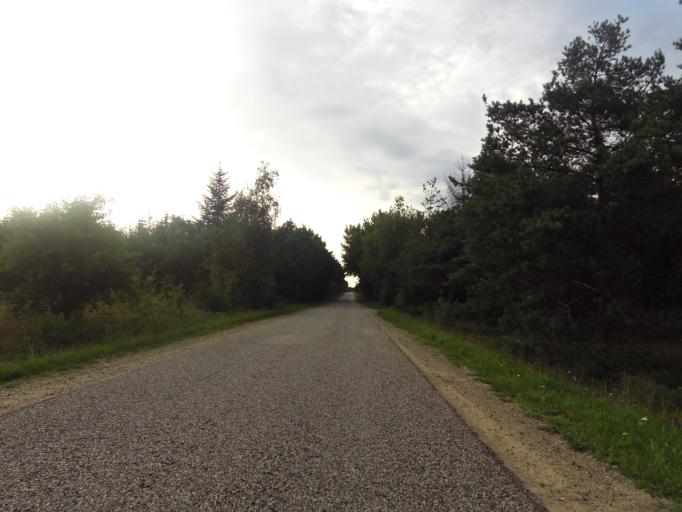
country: DK
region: South Denmark
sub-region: Tonder Kommune
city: Logumkloster
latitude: 55.1689
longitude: 8.9182
